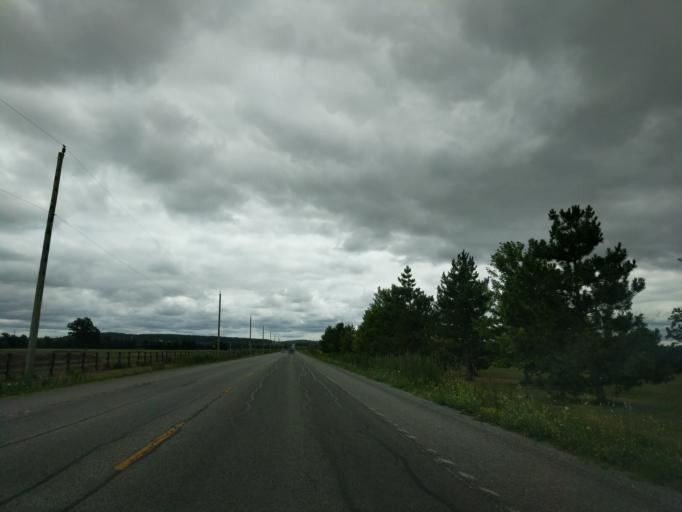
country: CA
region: Ontario
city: Thorold
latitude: 43.1778
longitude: -79.1689
